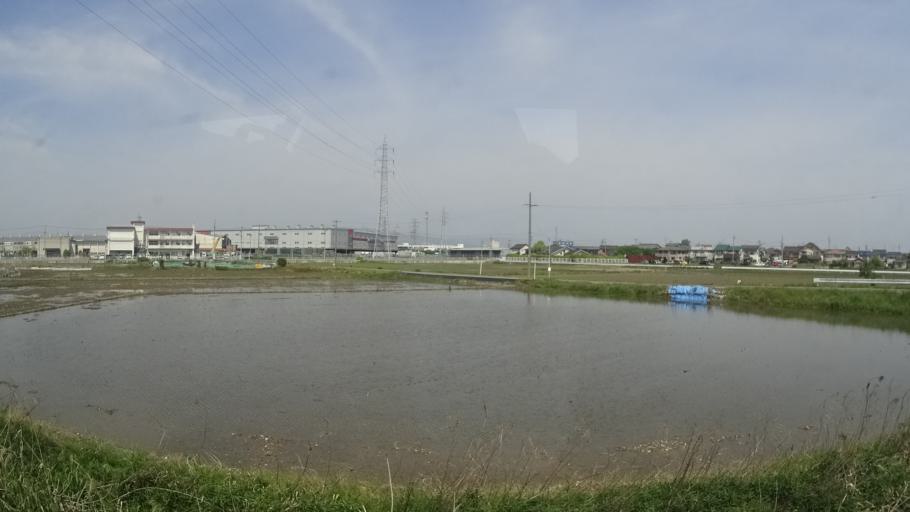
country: JP
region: Aichi
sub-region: Aisai-shi
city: Aisai
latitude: 35.1258
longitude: 136.7497
